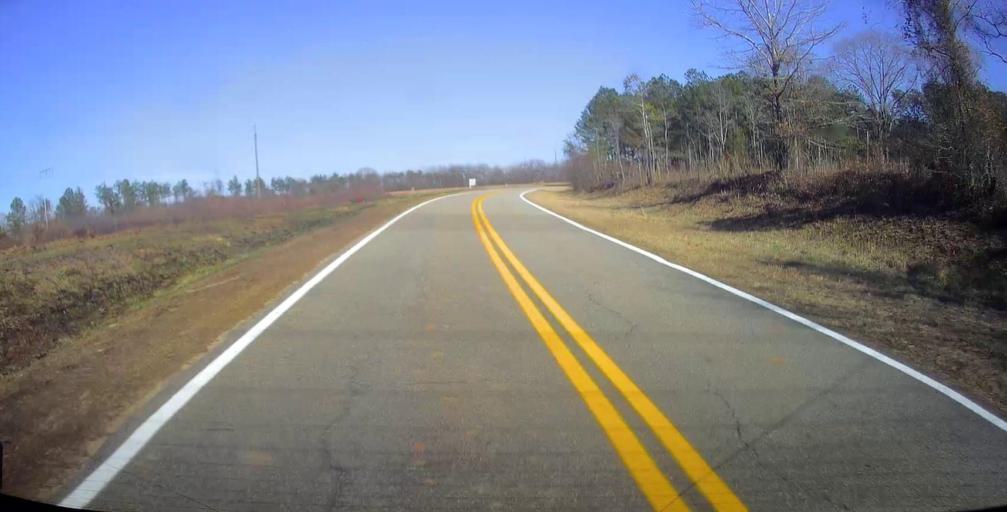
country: US
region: Georgia
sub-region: Peach County
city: Fort Valley
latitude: 32.6258
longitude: -83.9497
